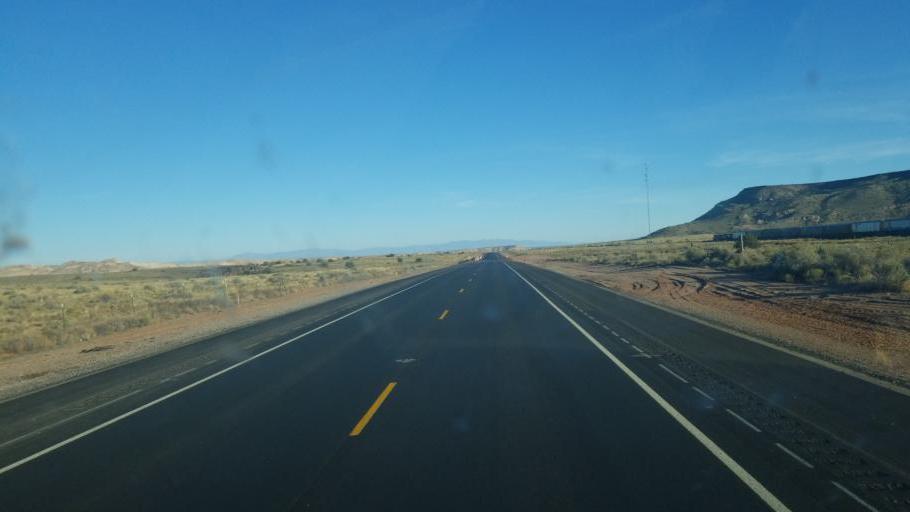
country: US
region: New Mexico
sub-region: Cibola County
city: Laguna
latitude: 34.9453
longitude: -107.1558
